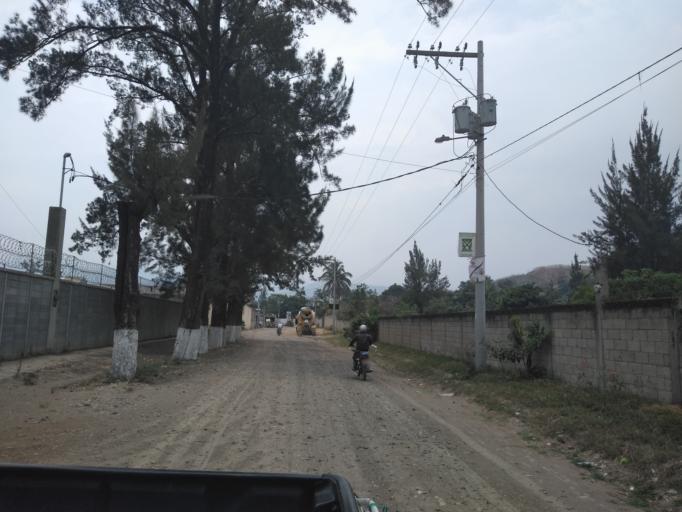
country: GT
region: Guatemala
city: Petapa
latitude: 14.5017
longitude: -90.5519
